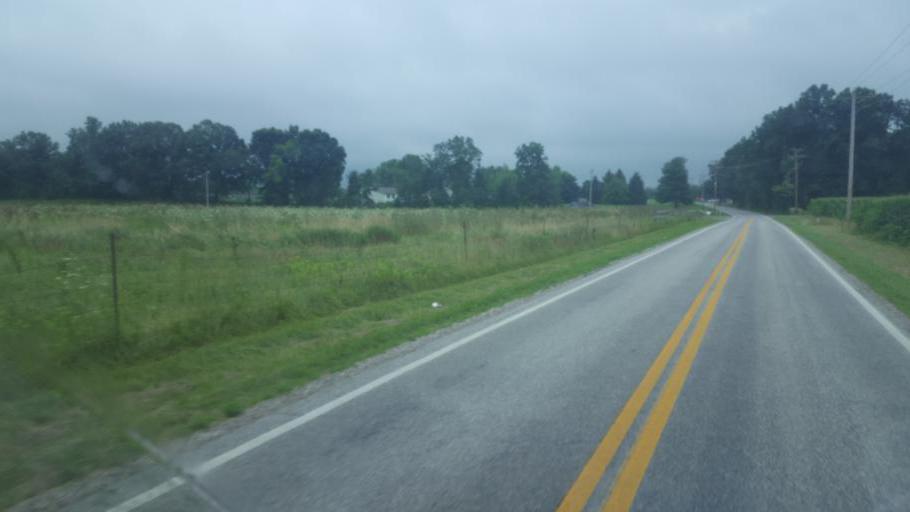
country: US
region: Ohio
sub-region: Delaware County
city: Sunbury
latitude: 40.2669
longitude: -82.8881
